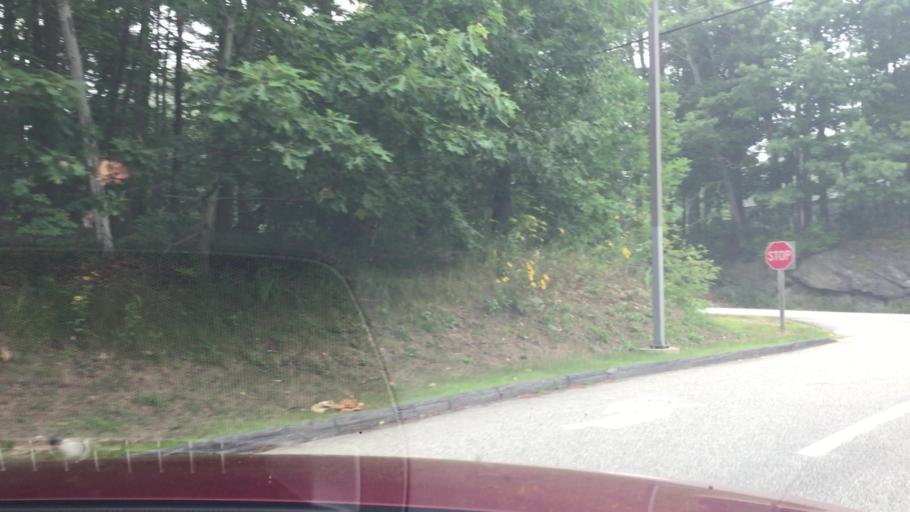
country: US
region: Maine
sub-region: Cumberland County
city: Freeport
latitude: 43.8609
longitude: -70.1037
